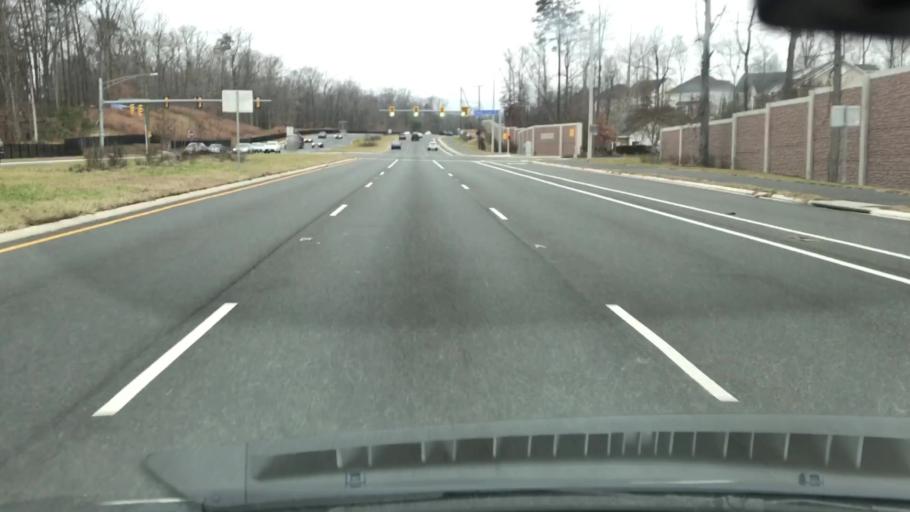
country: US
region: Virginia
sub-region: Fairfax County
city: Newington
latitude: 38.7075
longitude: -77.1818
